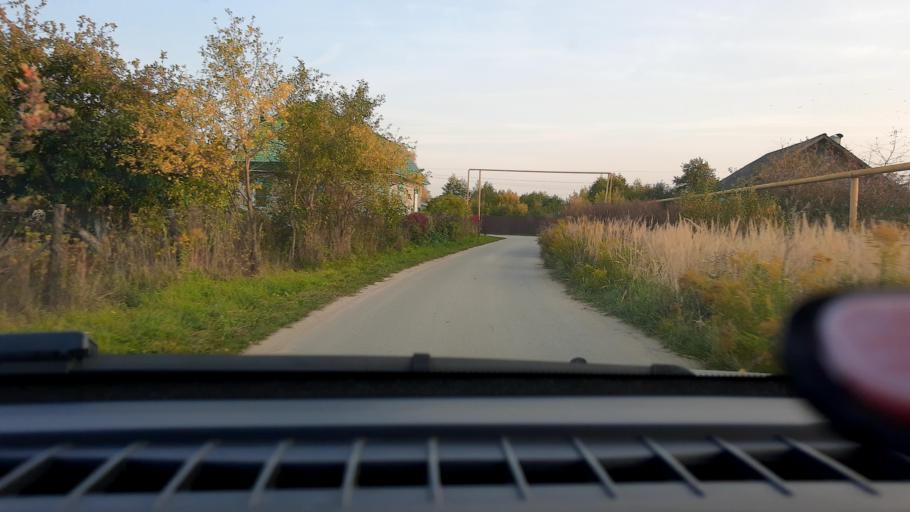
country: RU
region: Nizjnij Novgorod
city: Sitniki
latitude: 56.4043
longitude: 44.0410
